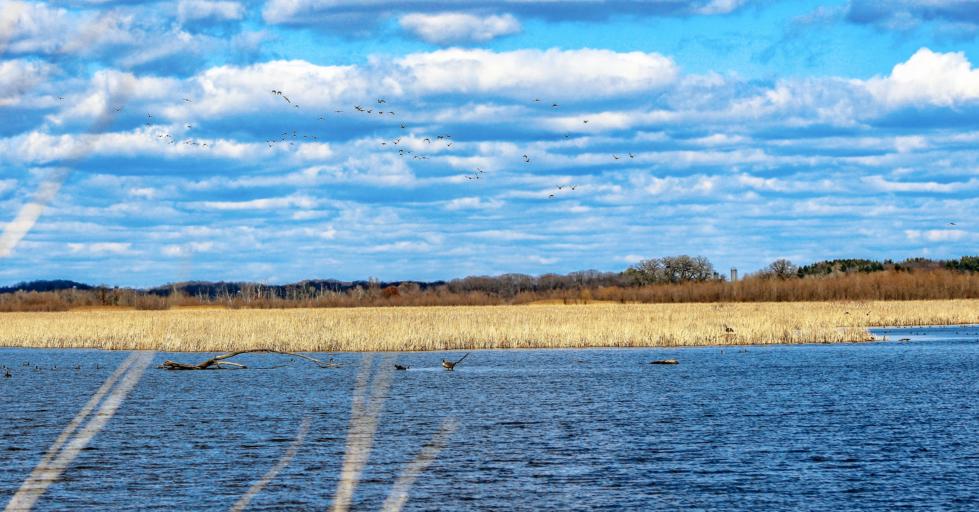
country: US
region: Wisconsin
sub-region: Jefferson County
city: Lake Ripley
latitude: 43.0455
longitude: -88.9880
